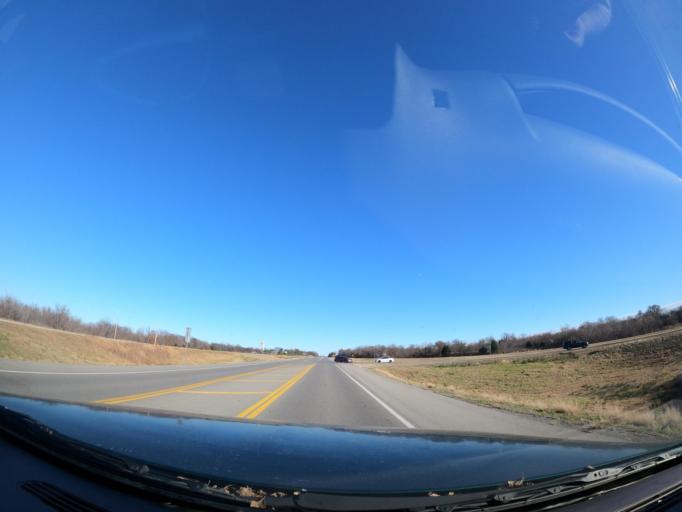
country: US
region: Oklahoma
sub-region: Pittsburg County
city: Longtown
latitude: 35.2392
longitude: -95.5491
